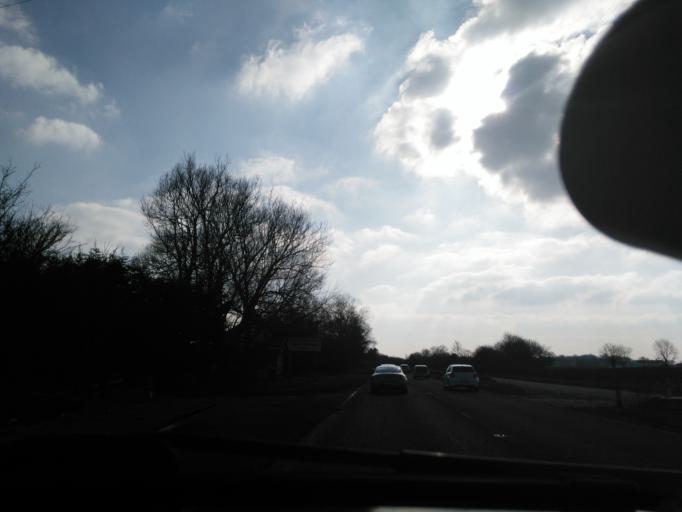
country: GB
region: England
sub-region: Wiltshire
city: Chippenham
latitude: 51.4926
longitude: -2.1273
